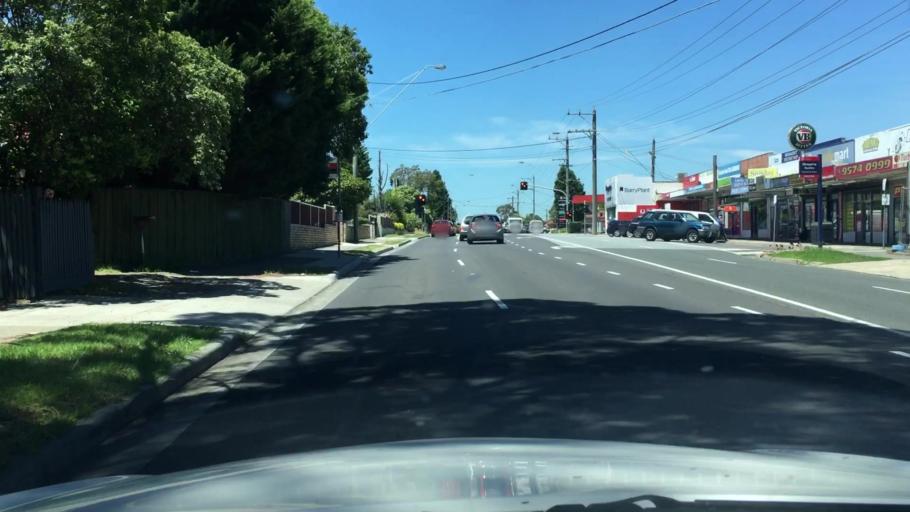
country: AU
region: Victoria
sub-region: Greater Dandenong
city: Noble Park North
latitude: -37.9665
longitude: 145.1861
